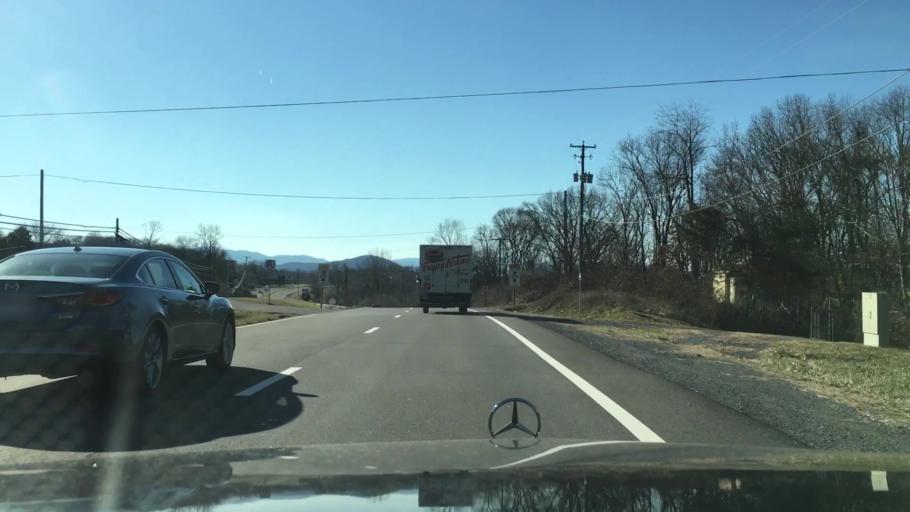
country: US
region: Virginia
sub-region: Roanoke County
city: Vinton
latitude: 37.2836
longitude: -79.8557
